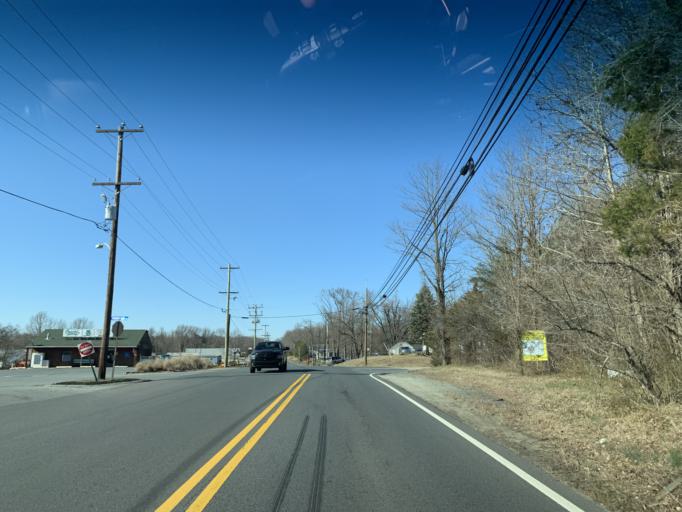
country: US
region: Maryland
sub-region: Cecil County
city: Elkton
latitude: 39.6211
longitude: -75.8515
